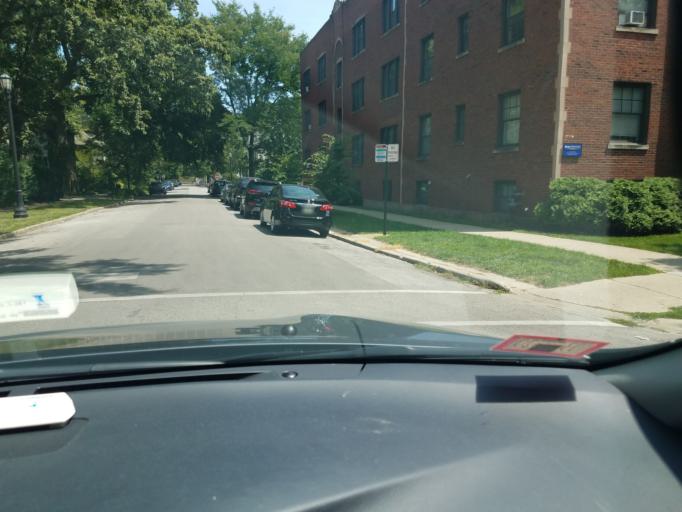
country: US
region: Illinois
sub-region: Cook County
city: Evanston
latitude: 42.0394
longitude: -87.6851
